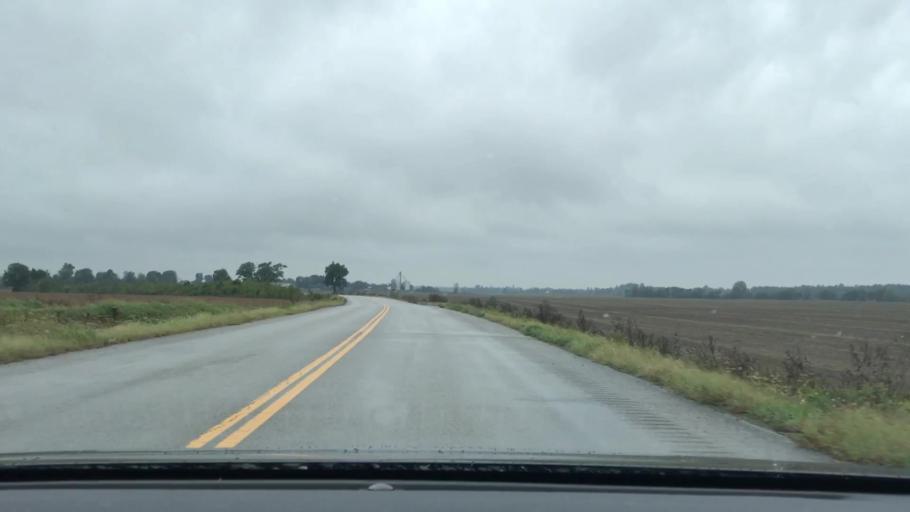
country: US
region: Kentucky
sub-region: Hopkins County
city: Madisonville
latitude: 37.3822
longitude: -87.3397
